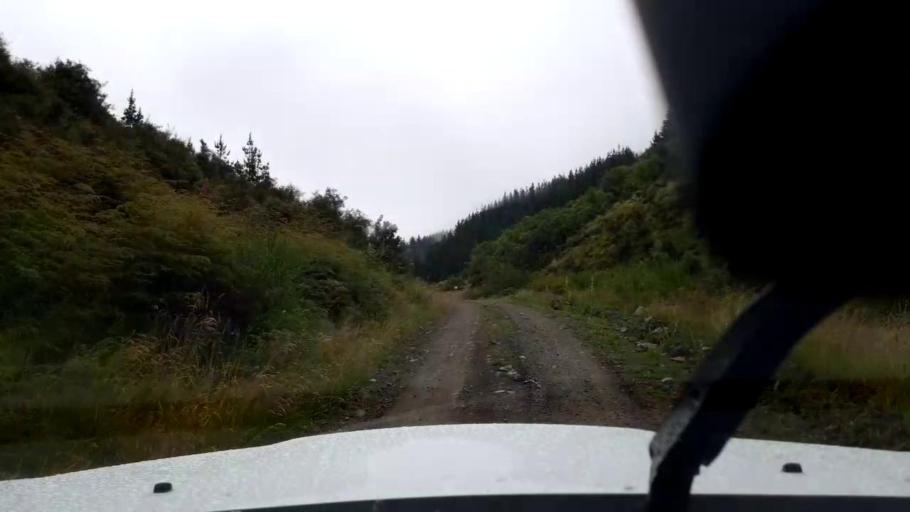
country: NZ
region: Canterbury
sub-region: Timaru District
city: Pleasant Point
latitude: -44.0340
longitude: 170.9926
